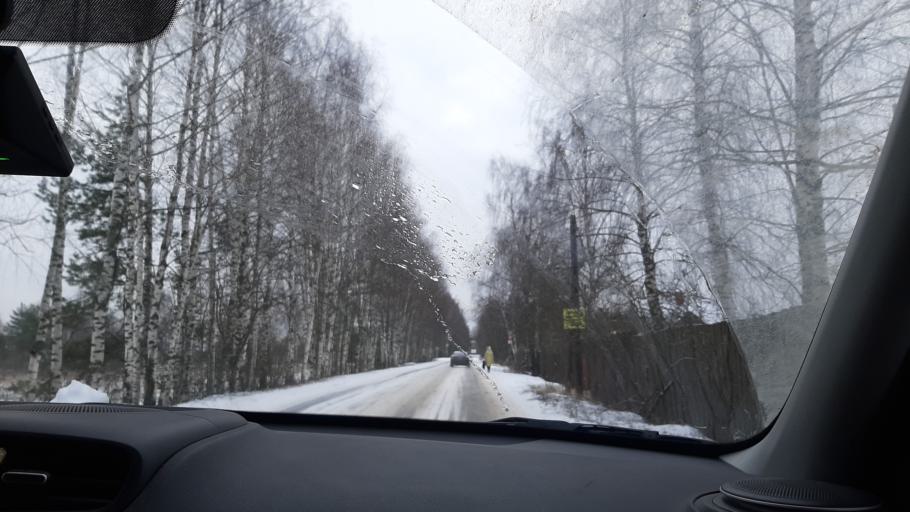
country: RU
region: Ivanovo
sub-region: Gorod Ivanovo
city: Ivanovo
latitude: 56.9324
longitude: 40.9748
